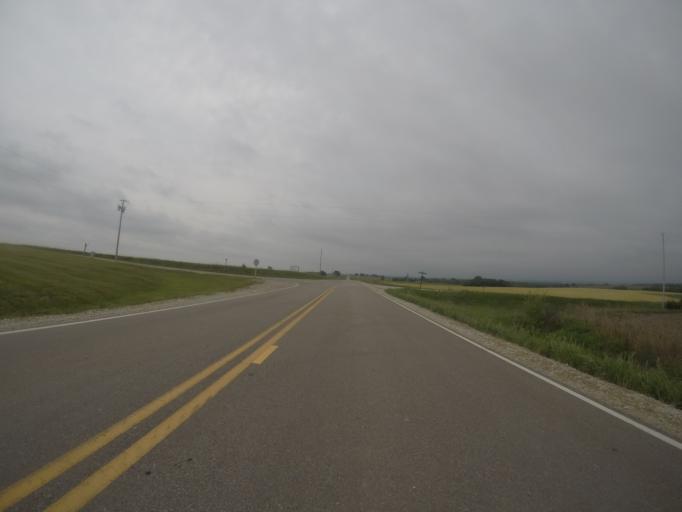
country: US
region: Kansas
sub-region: Pottawatomie County
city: Westmoreland
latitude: 39.5116
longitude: -96.2219
